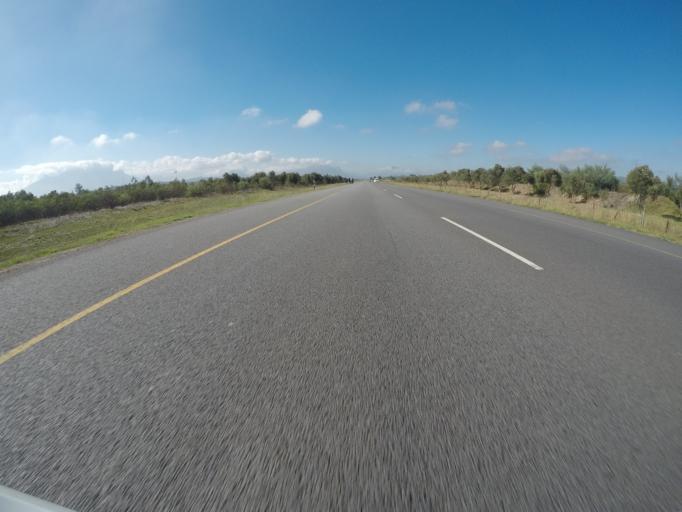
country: ZA
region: Western Cape
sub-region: City of Cape Town
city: Kraaifontein
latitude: -33.8509
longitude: 18.8056
